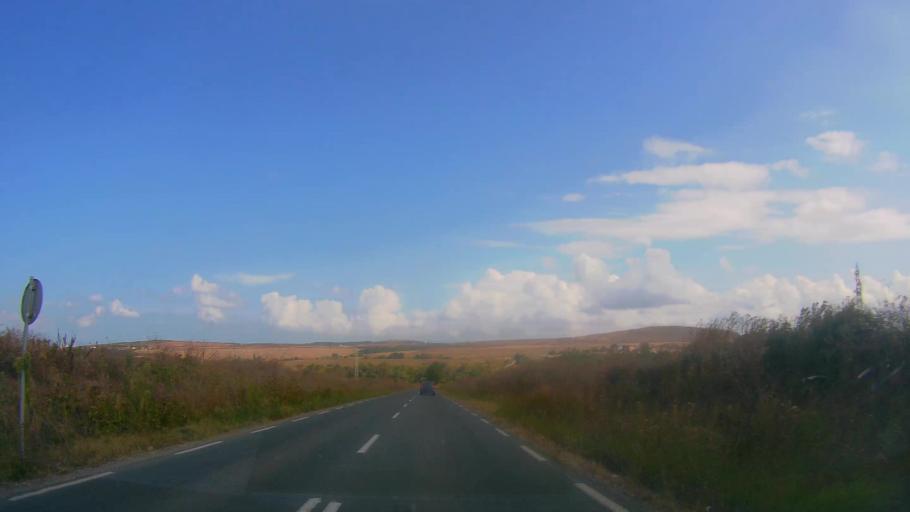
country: BG
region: Burgas
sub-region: Obshtina Kameno
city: Kameno
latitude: 42.4774
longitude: 27.3531
